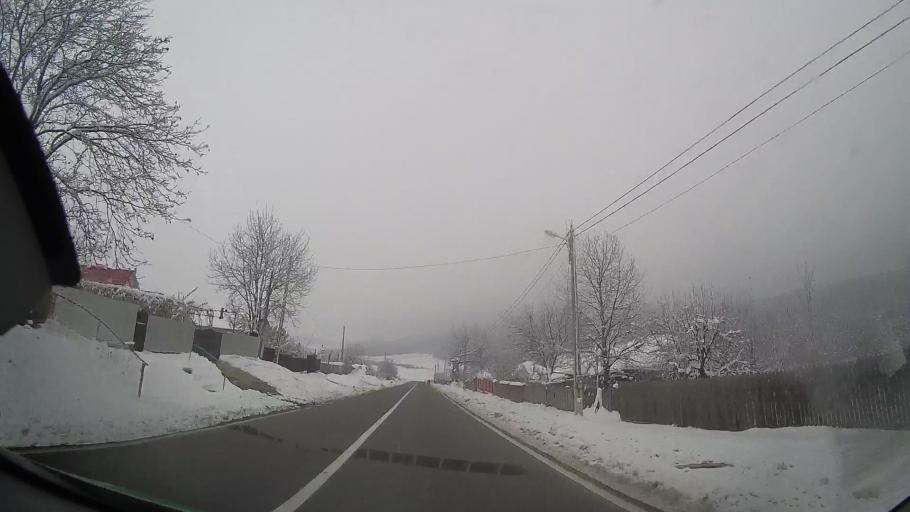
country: RO
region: Neamt
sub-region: Comuna Poenari
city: Poienari
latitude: 46.8761
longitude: 27.1347
